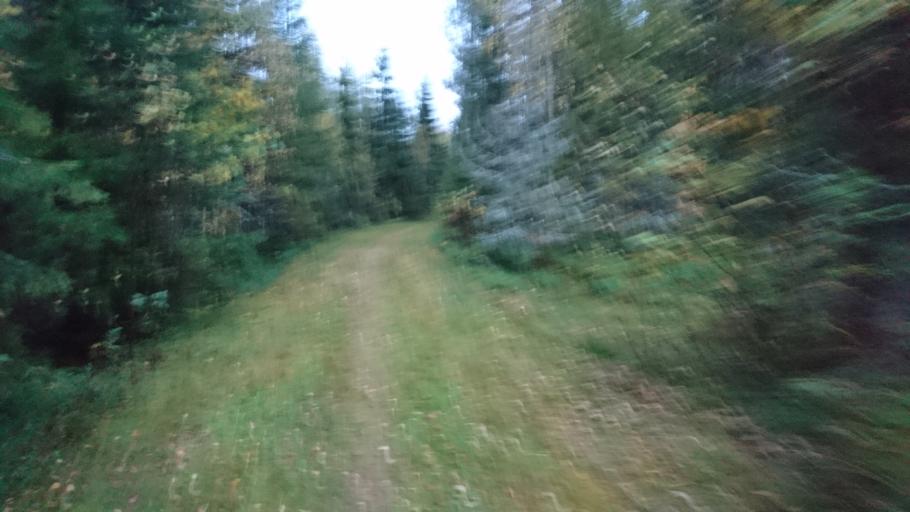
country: SE
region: Vaesterbotten
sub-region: Robertsfors Kommun
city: Robertsfors
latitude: 64.2310
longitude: 20.9948
